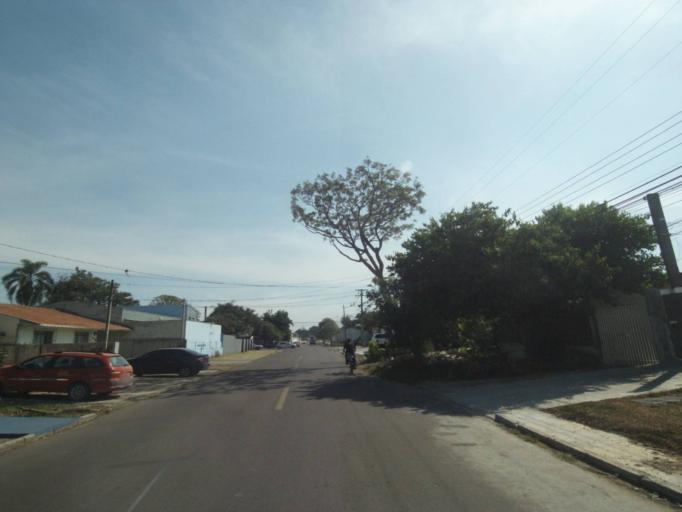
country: BR
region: Parana
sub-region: Sao Jose Dos Pinhais
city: Sao Jose dos Pinhais
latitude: -25.4876
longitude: -49.2366
